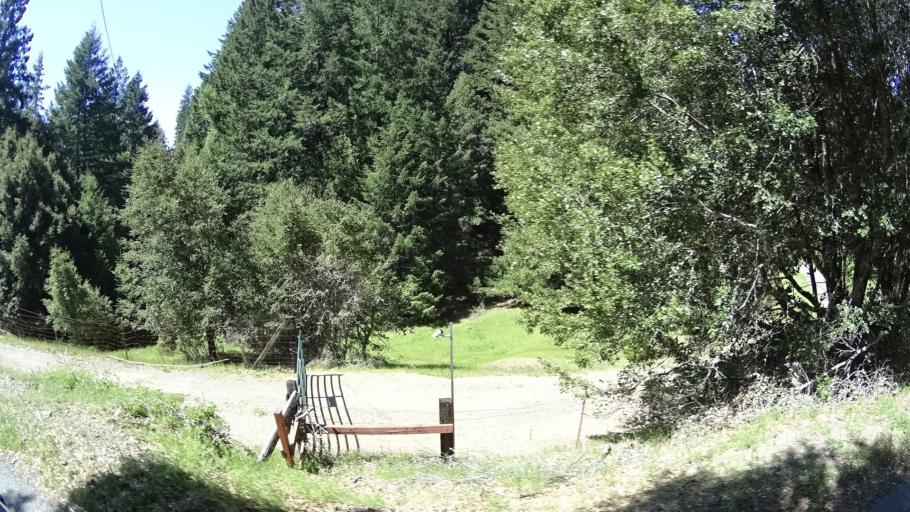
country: US
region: California
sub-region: Humboldt County
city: Redway
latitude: 40.1418
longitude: -124.0054
